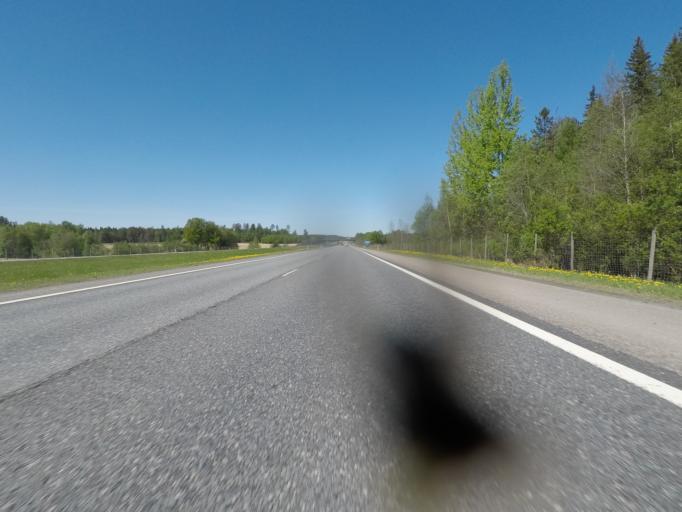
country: FI
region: Haeme
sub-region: Haemeenlinna
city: Tervakoski
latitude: 60.8409
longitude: 24.6371
